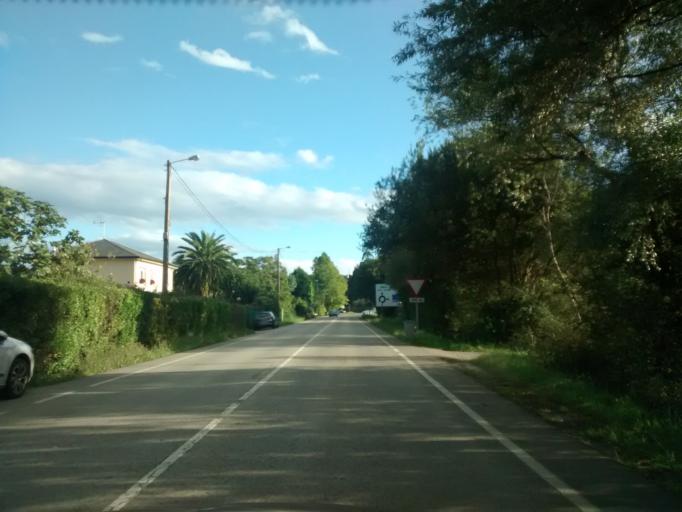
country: ES
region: Cantabria
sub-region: Provincia de Cantabria
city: Miengo
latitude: 43.4169
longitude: -3.9593
